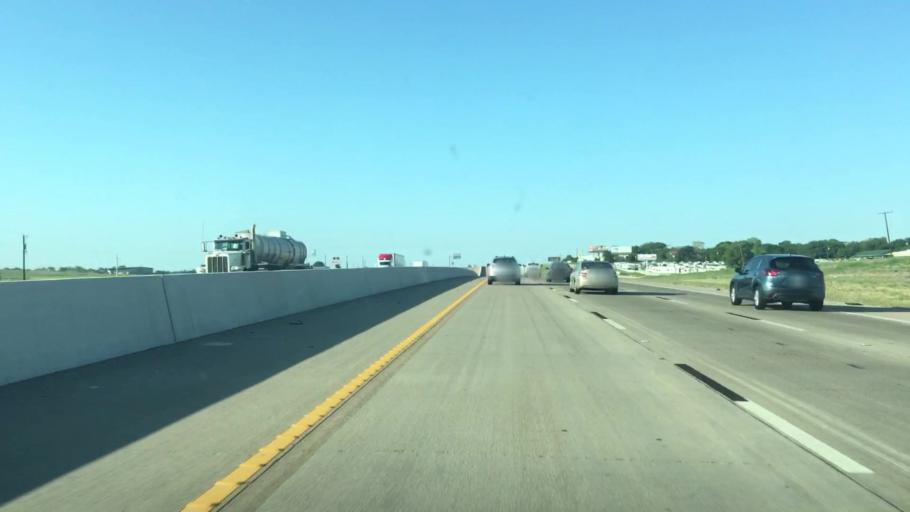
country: US
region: Texas
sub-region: McLennan County
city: Hewitt
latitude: 31.4352
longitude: -97.1864
